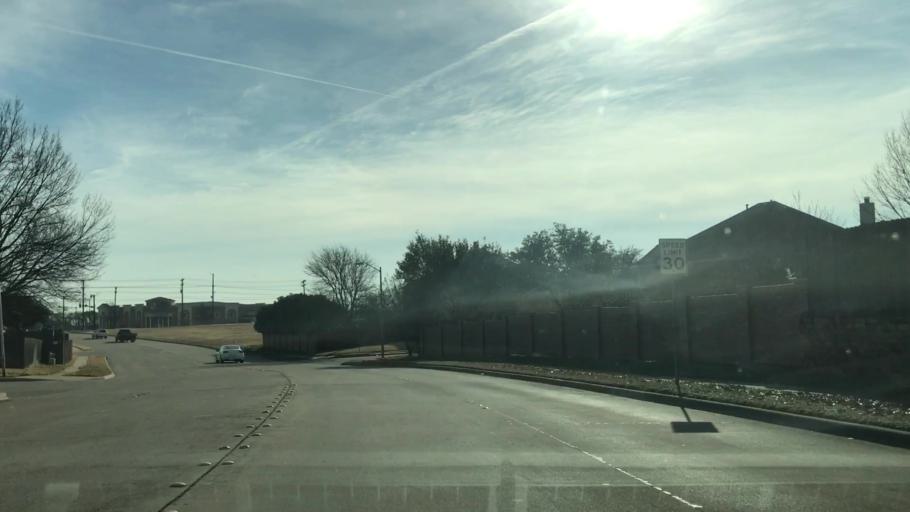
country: US
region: Texas
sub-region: Tarrant County
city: Colleyville
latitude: 32.8918
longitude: -97.2059
